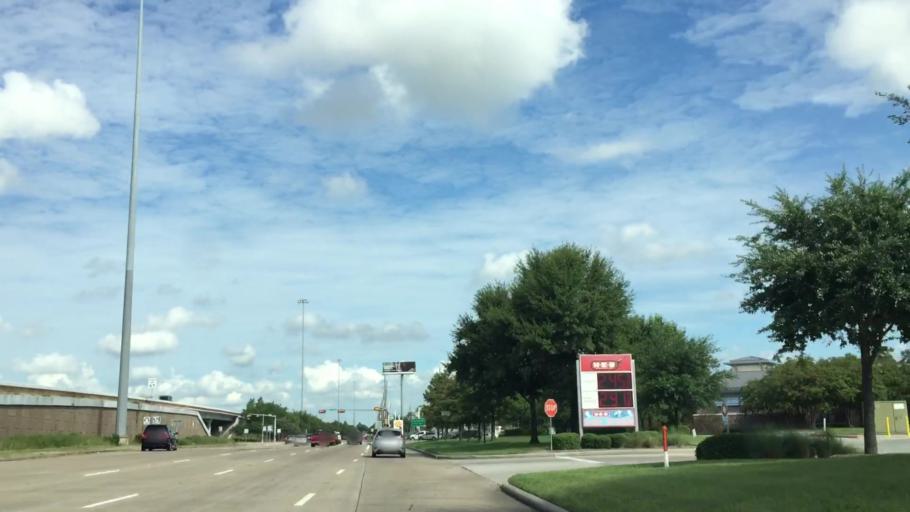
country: US
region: Texas
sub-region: Harris County
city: Oak Cliff Place
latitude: 29.9954
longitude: -95.5773
